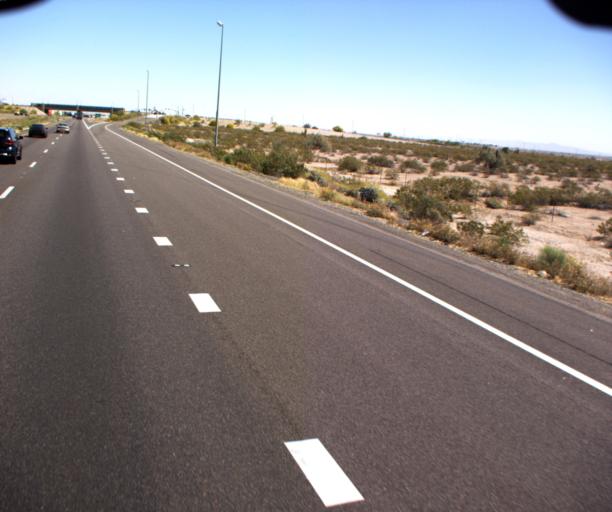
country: US
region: Arizona
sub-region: Maricopa County
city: Citrus Park
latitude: 33.4591
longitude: -112.5112
